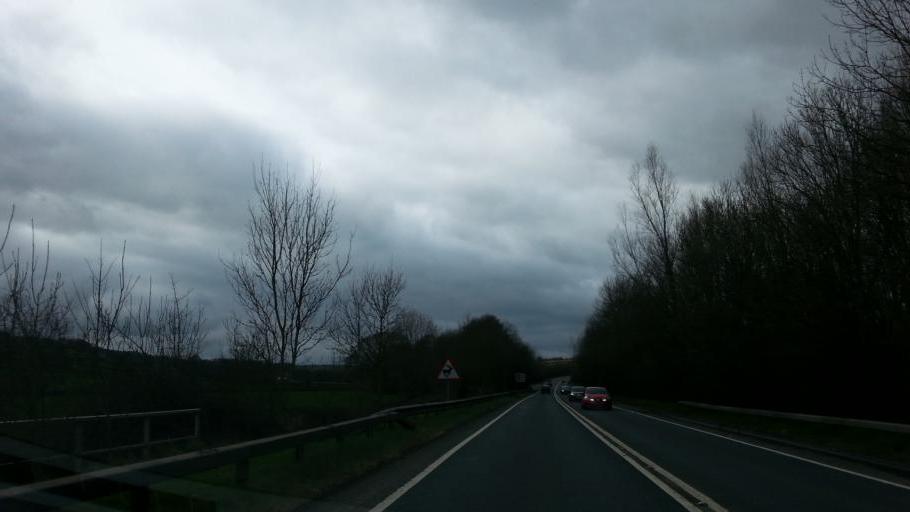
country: GB
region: England
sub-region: Devon
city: Tiverton
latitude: 50.9152
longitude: -3.5045
